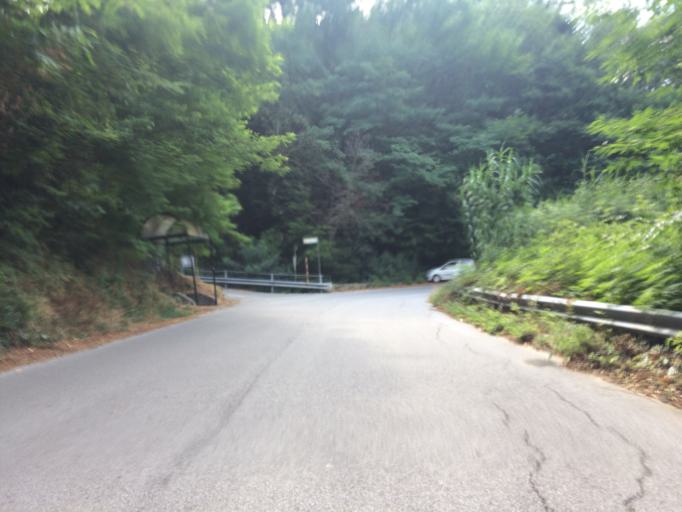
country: IT
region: Liguria
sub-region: Provincia di Savona
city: San Giovanni
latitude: 44.4010
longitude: 8.4937
